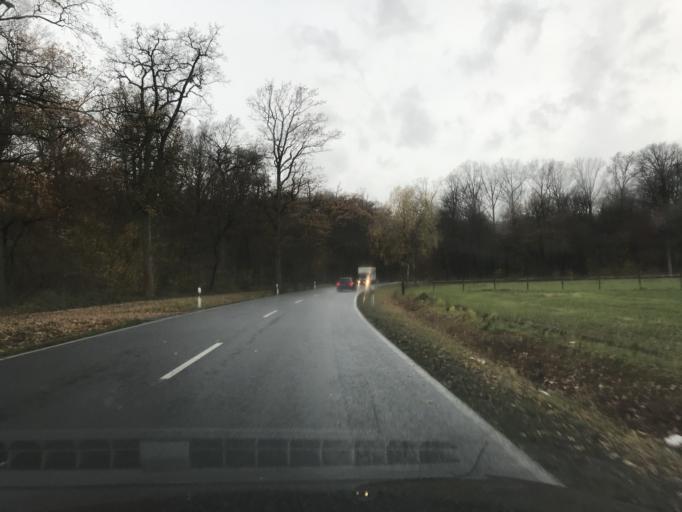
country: DE
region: North Rhine-Westphalia
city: Oelde
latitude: 51.8437
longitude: 8.1623
